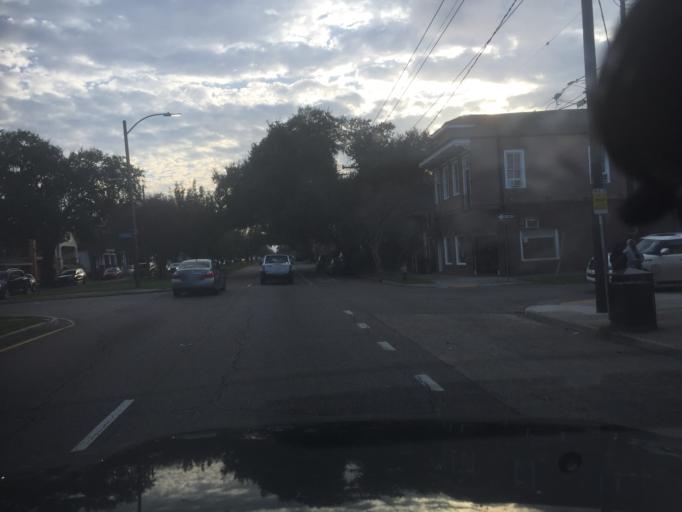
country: US
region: Louisiana
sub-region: Orleans Parish
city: New Orleans
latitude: 29.9811
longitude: -90.0738
